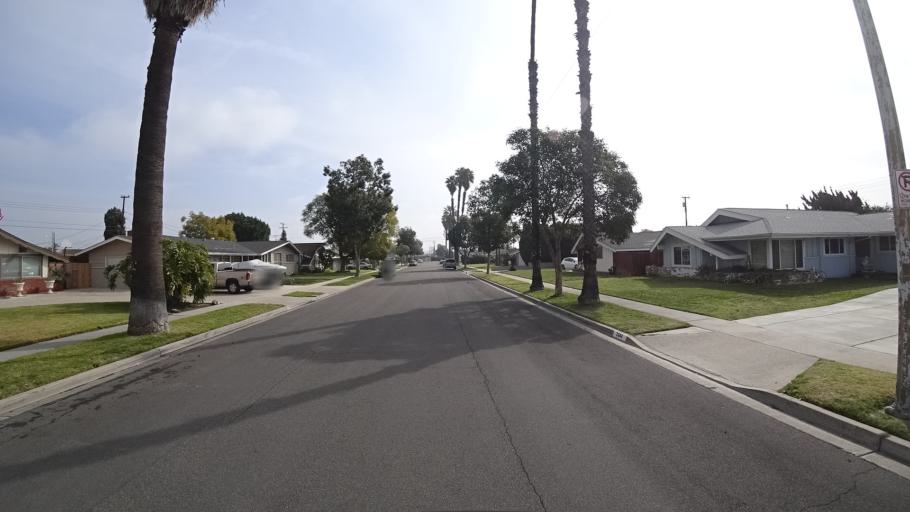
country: US
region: California
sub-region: Orange County
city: Stanton
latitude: 33.8132
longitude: -117.9784
